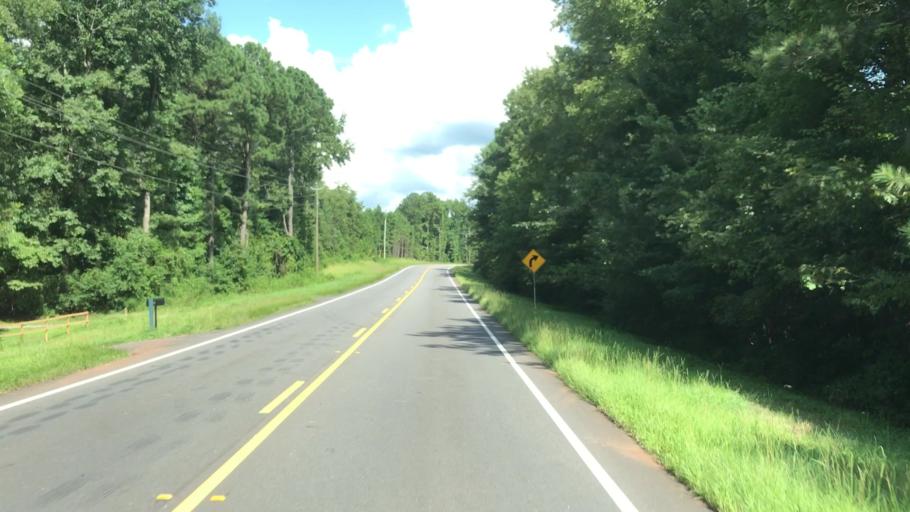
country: US
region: Georgia
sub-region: Newton County
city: Oxford
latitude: 33.6534
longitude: -83.8449
